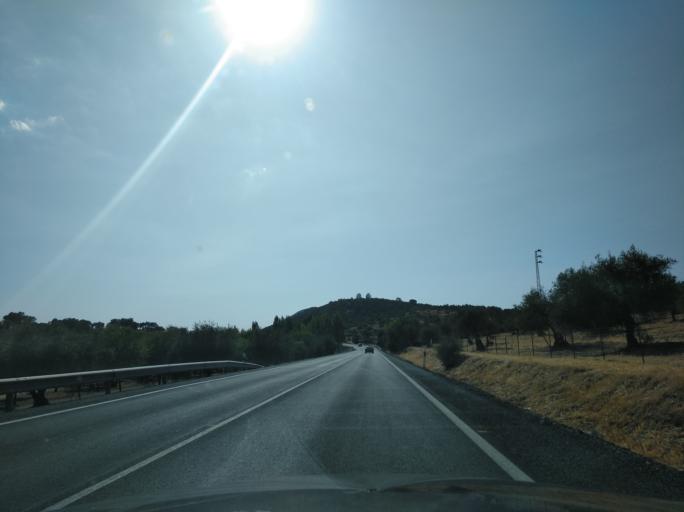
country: ES
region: Andalusia
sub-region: Provincia de Huelva
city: Rosal de la Frontera
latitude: 37.9655
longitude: -7.2314
